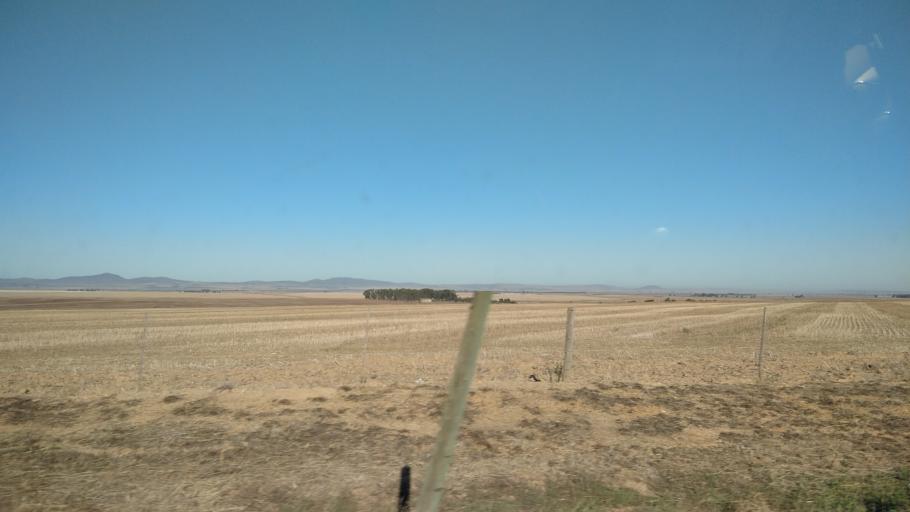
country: ZA
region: Western Cape
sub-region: West Coast District Municipality
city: Malmesbury
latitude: -33.3282
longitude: 18.6297
